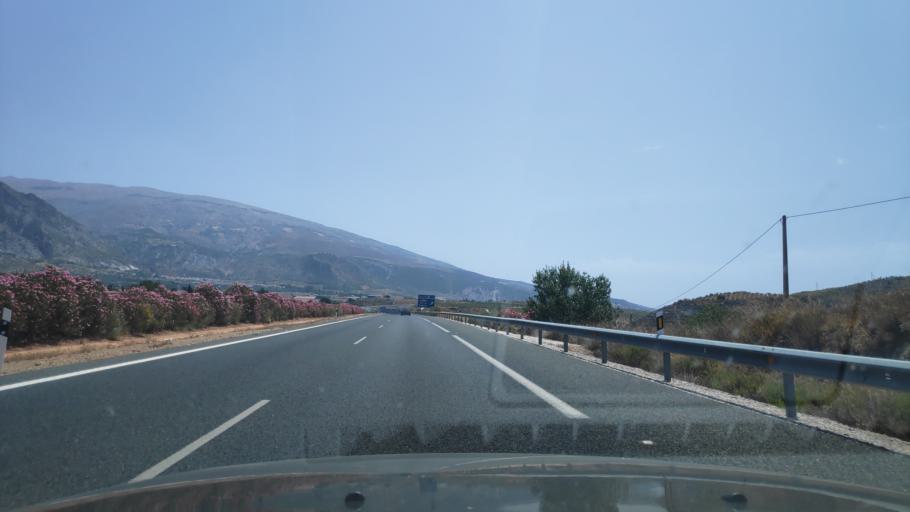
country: ES
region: Andalusia
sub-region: Provincia de Granada
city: Durcal
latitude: 36.9820
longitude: -3.5778
